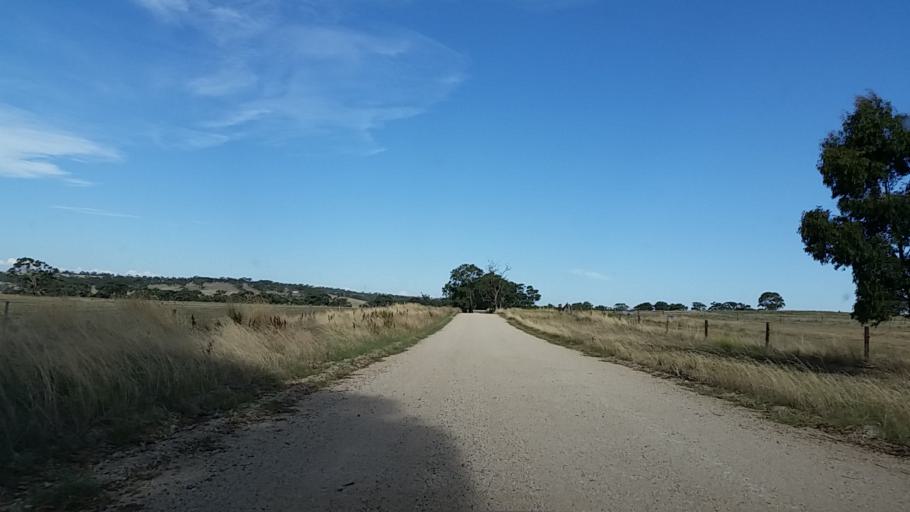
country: AU
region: South Australia
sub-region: Barossa
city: Angaston
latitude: -34.5825
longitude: 139.1522
